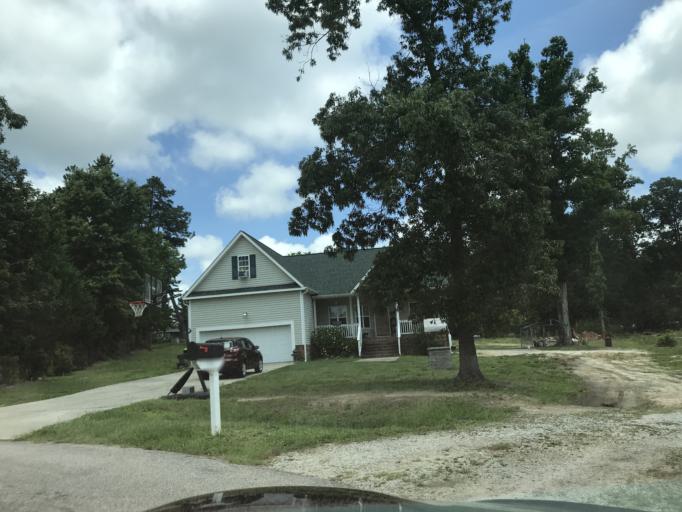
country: US
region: North Carolina
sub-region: Wake County
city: Rolesville
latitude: 35.9477
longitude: -78.3739
